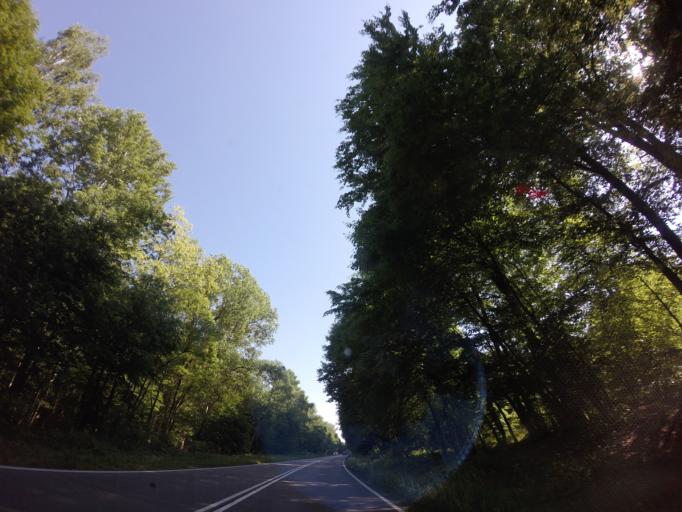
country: PL
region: West Pomeranian Voivodeship
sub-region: Powiat gryfinski
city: Stare Czarnowo
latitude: 53.3196
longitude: 14.7908
